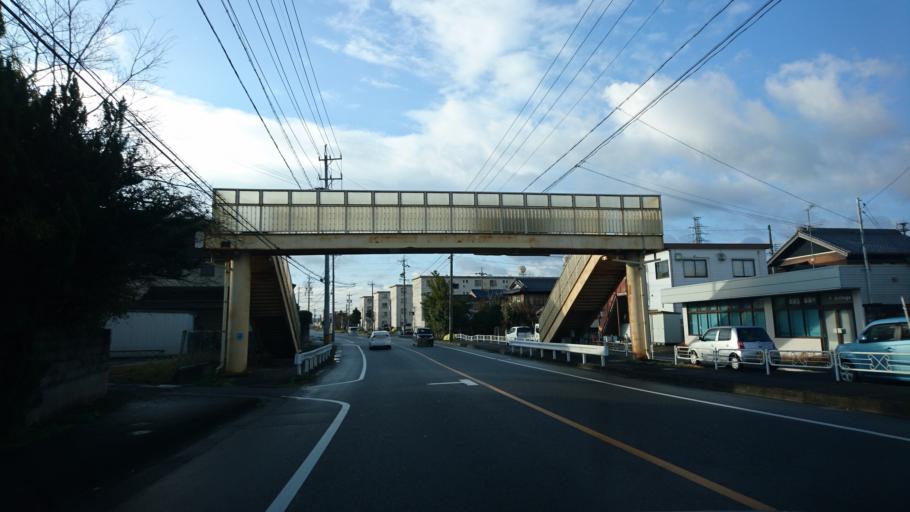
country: JP
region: Mie
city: Ueno-ebisumachi
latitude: 34.7550
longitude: 136.1232
